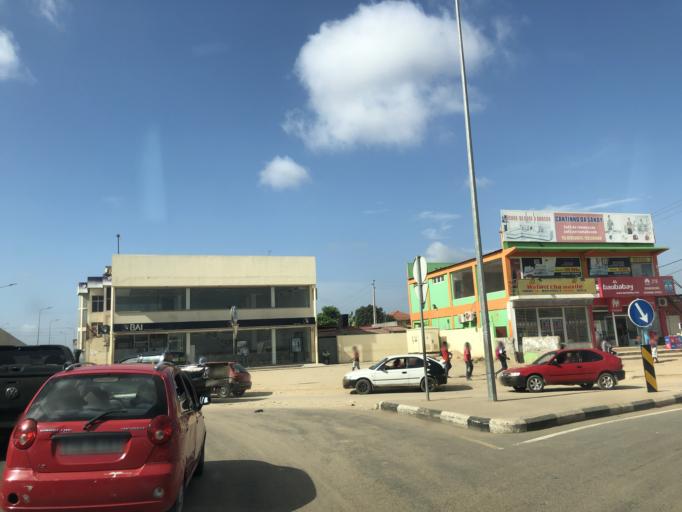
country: AO
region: Luanda
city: Luanda
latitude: -8.9020
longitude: 13.2612
